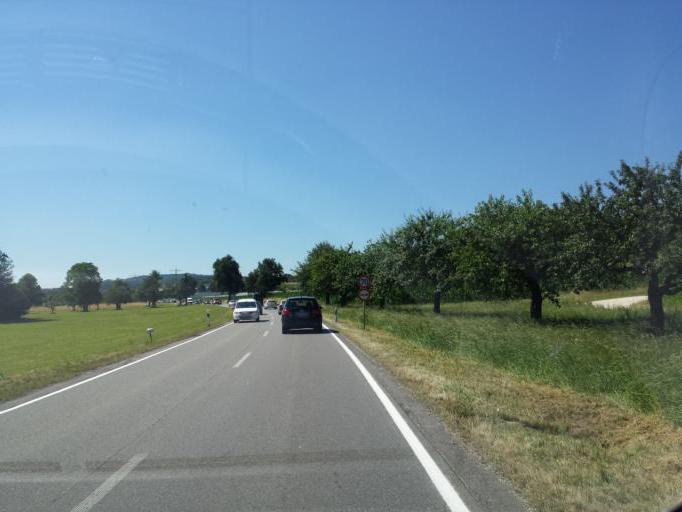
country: DE
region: Baden-Wuerttemberg
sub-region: Tuebingen Region
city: Owingen
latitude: 47.7911
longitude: 9.1601
